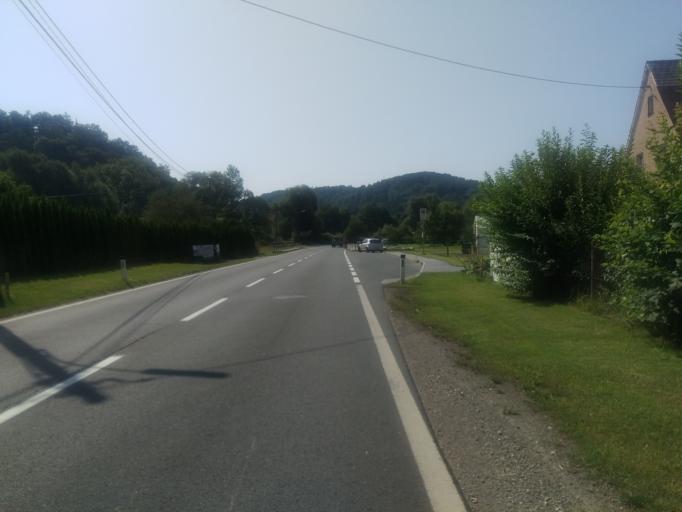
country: AT
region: Styria
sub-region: Politischer Bezirk Graz-Umgebung
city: Fernitz
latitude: 46.9578
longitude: 15.5072
